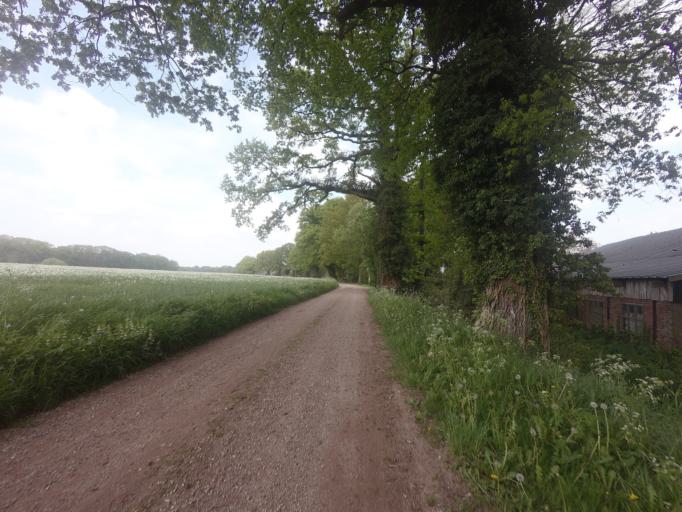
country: NL
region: Overijssel
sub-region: Gemeente Hof van Twente
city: Delden
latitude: 52.2122
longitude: 6.7314
